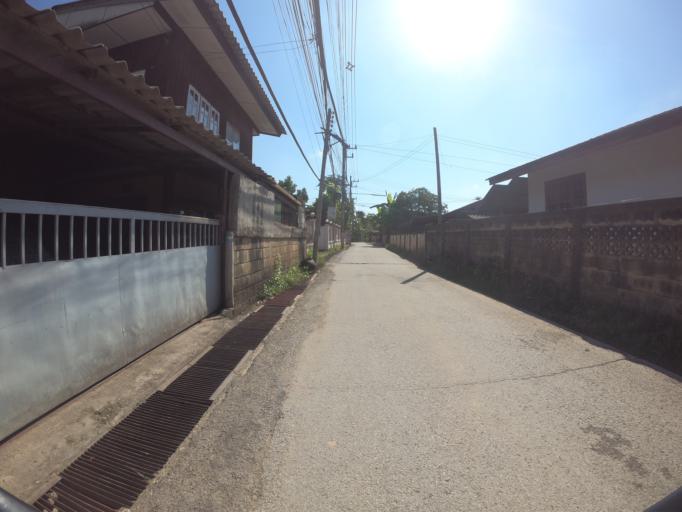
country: TH
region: Chiang Mai
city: Chiang Mai
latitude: 18.7606
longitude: 98.9564
